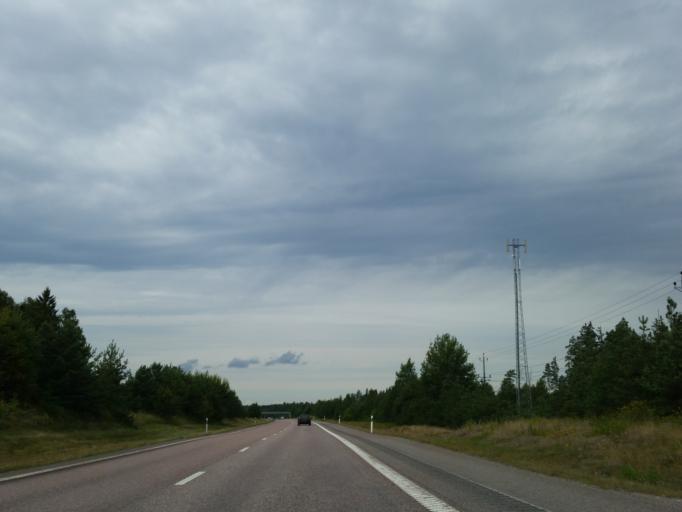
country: SE
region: Stockholm
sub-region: Nykvarns Kommun
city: Nykvarn
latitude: 59.2102
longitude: 17.3327
